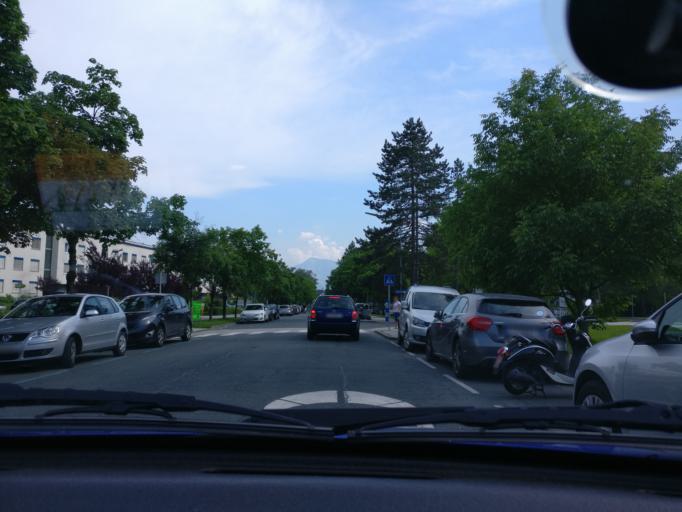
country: AT
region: Carinthia
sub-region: Klagenfurt am Woerthersee
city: Klagenfurt am Woerthersee
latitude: 46.6176
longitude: 14.2674
